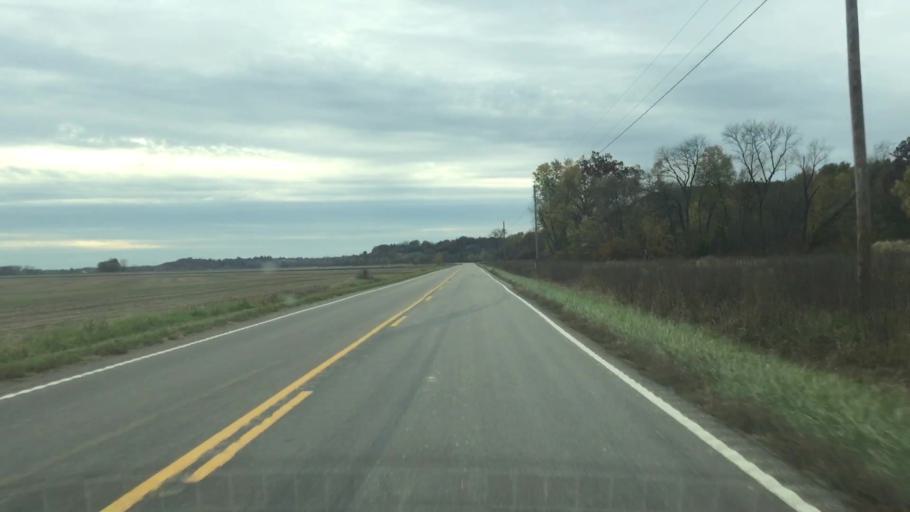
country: US
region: Missouri
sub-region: Callaway County
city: Fulton
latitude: 38.7075
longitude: -91.7858
